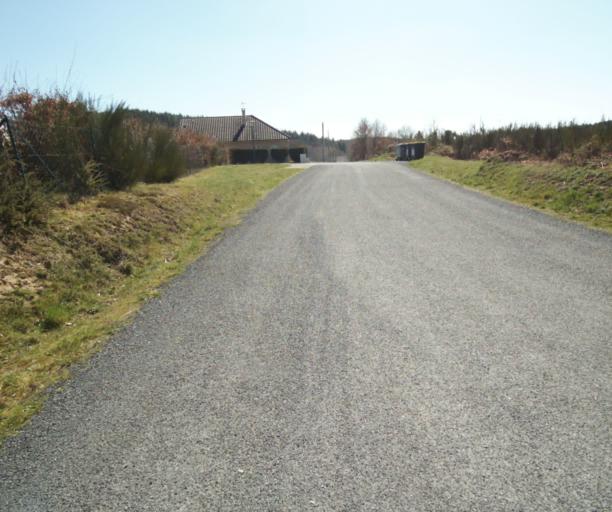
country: FR
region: Limousin
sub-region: Departement de la Correze
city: Saint-Mexant
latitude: 45.2782
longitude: 1.6538
